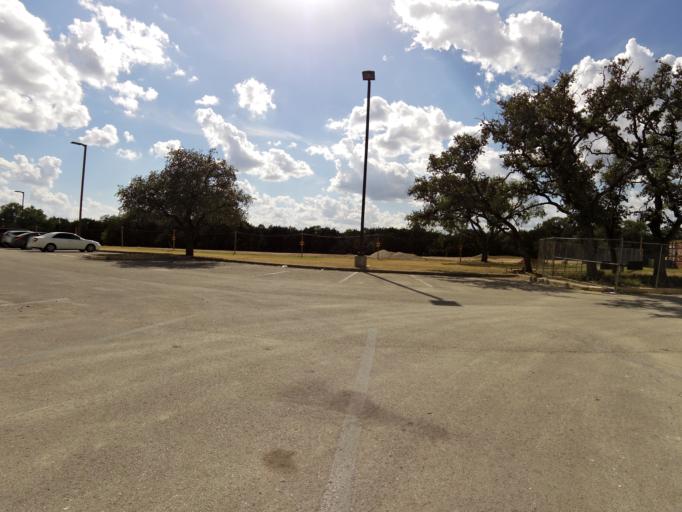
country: US
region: Texas
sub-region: Bexar County
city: Helotes
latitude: 29.5853
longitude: -98.6290
